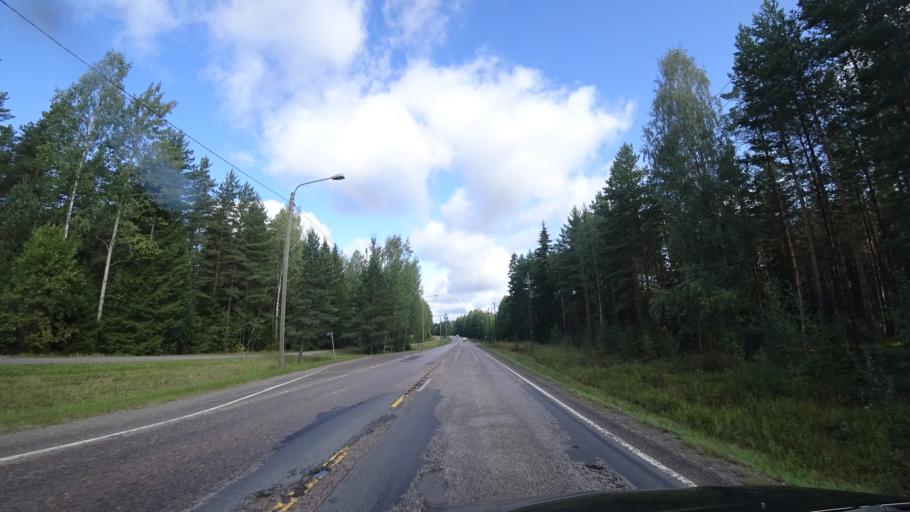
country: FI
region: Uusimaa
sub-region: Helsinki
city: Tuusula
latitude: 60.4265
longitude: 24.9963
